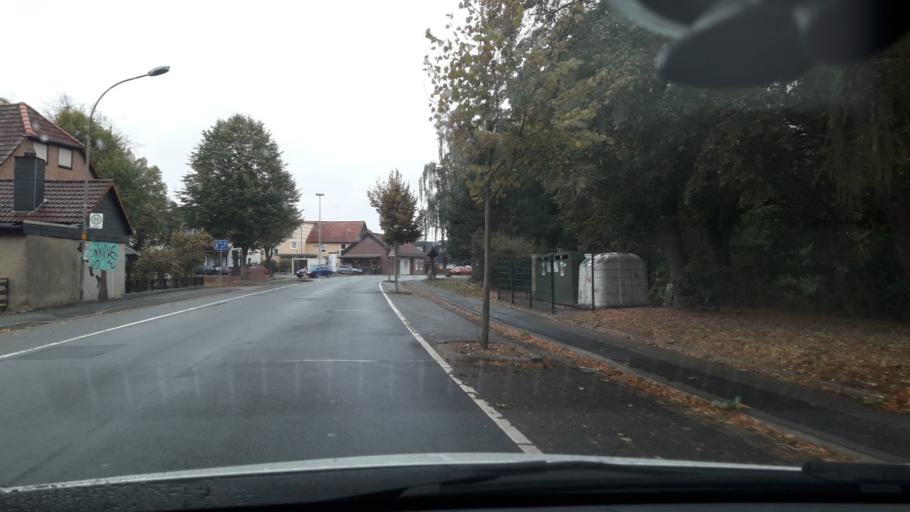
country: DE
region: Lower Saxony
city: Vienenburg
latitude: 51.9613
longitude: 10.5832
